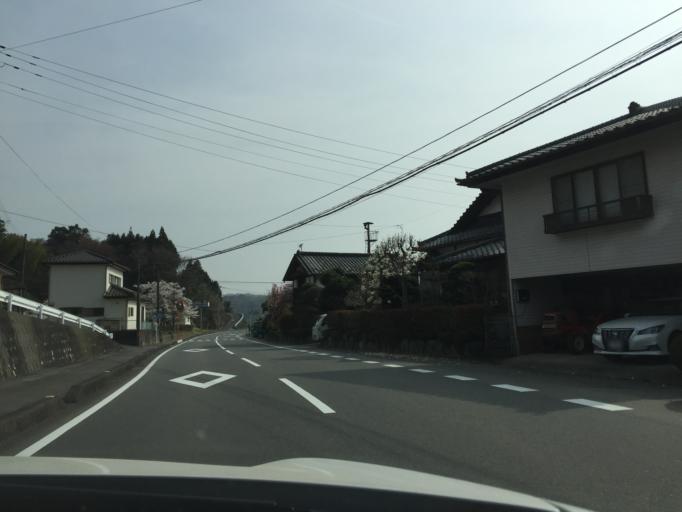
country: JP
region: Fukushima
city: Iwaki
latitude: 36.9792
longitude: 140.8010
